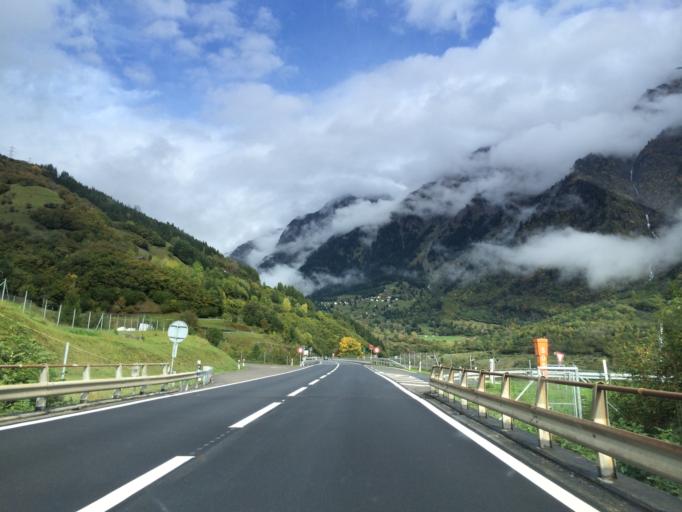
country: CH
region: Grisons
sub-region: Moesa District
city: Mesocco
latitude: 46.3988
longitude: 9.2291
